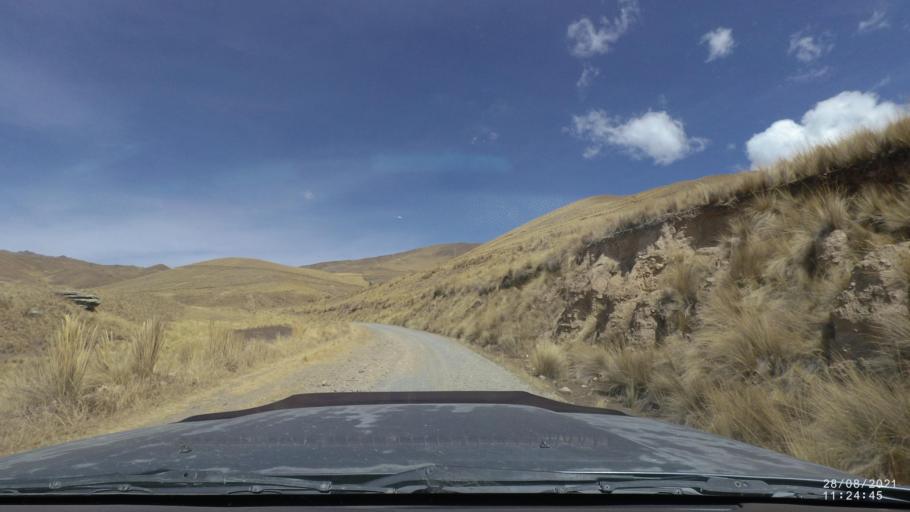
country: BO
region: Cochabamba
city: Sipe Sipe
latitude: -17.1686
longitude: -66.3515
